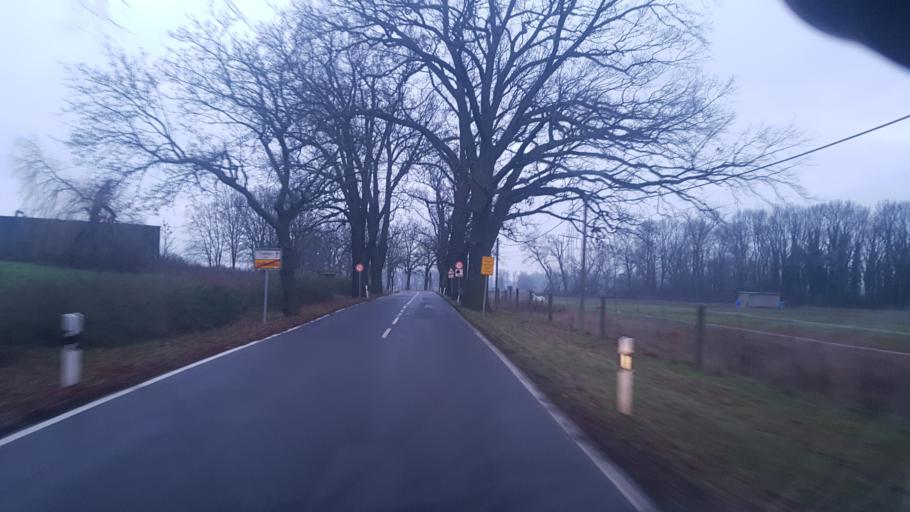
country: DE
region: Brandenburg
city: Trebbin
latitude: 52.2486
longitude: 13.2110
